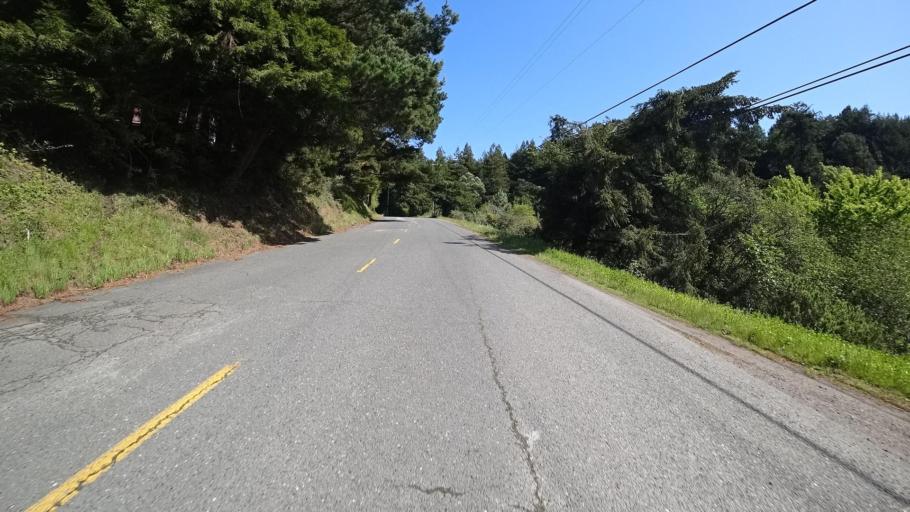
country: US
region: California
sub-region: Humboldt County
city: Hydesville
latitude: 40.5694
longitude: -124.1208
